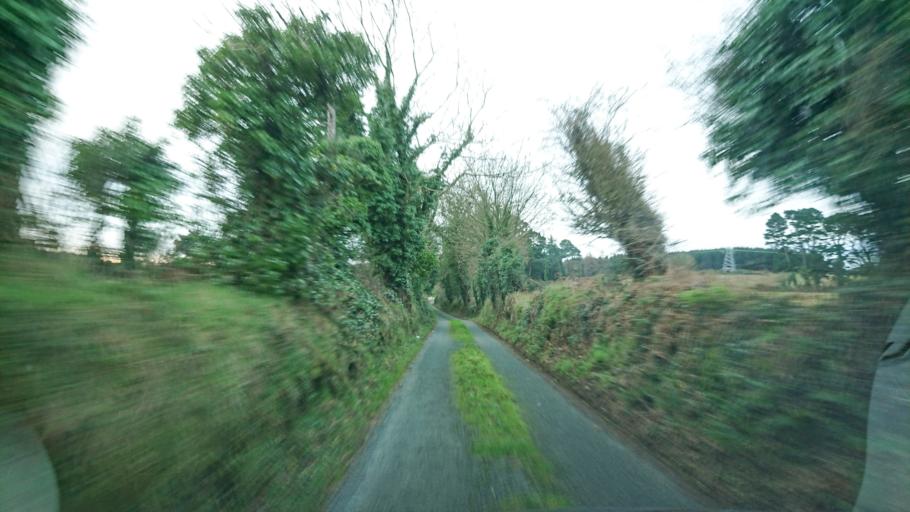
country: IE
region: Leinster
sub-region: Kilkenny
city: Mooncoin
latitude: 52.2178
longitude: -7.2713
